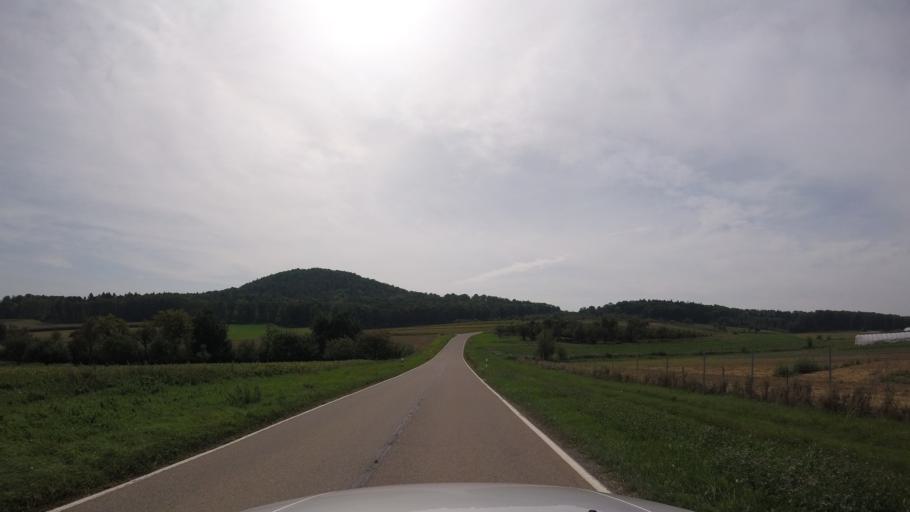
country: DE
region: Baden-Wuerttemberg
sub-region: Regierungsbezirk Stuttgart
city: Ilsfeld
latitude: 49.0370
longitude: 9.2726
